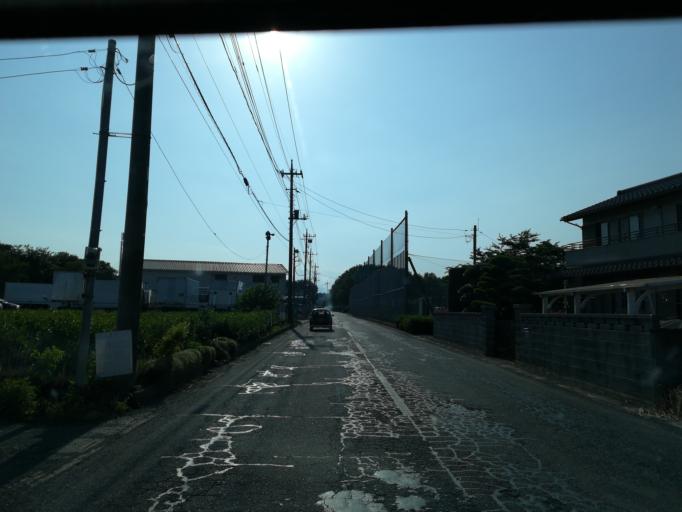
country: JP
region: Saitama
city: Sayama
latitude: 35.8018
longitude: 139.3894
